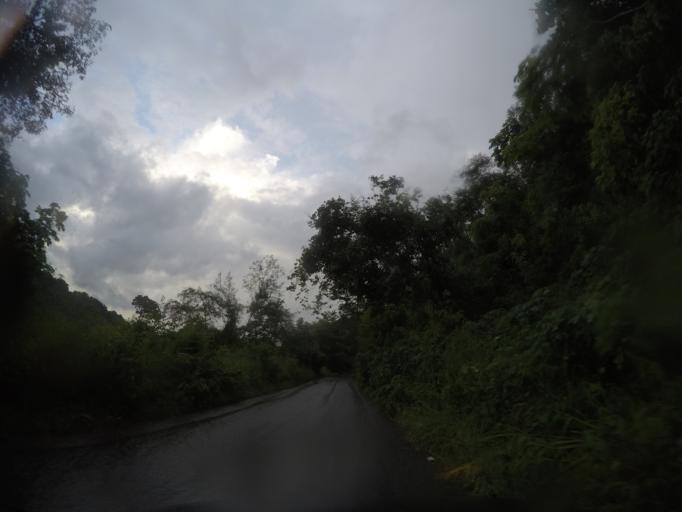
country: MX
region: Oaxaca
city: San Gabriel Mixtepec
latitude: 16.0566
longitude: -97.0805
